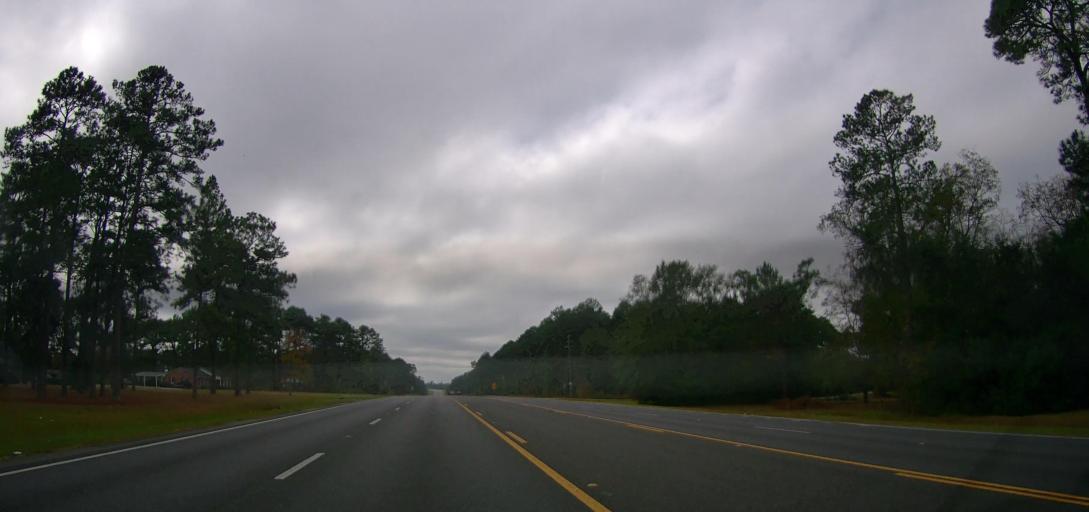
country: US
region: Georgia
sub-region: Colquitt County
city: Moultrie
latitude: 31.0911
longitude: -83.8066
